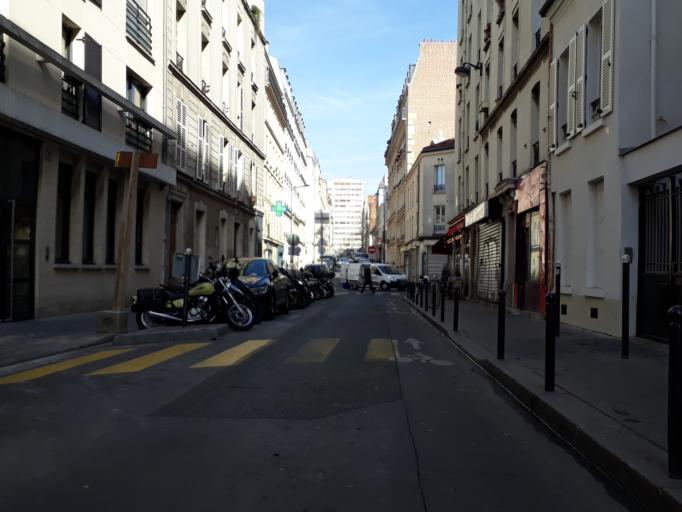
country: FR
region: Ile-de-France
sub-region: Paris
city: Saint-Ouen
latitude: 48.8934
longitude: 2.3219
